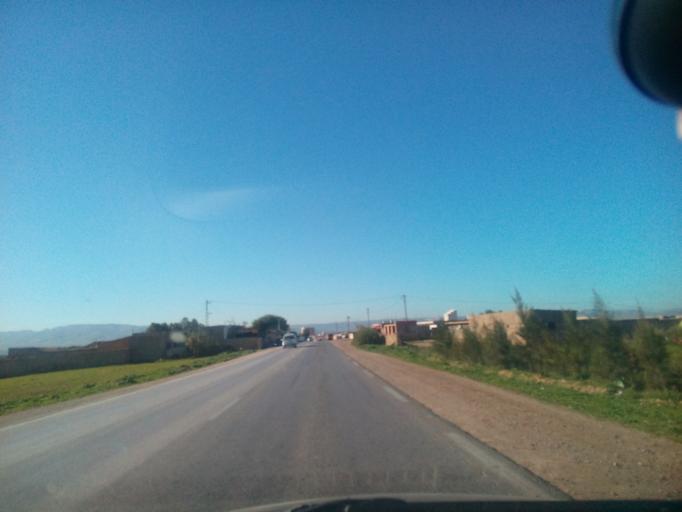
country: DZ
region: Relizane
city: Relizane
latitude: 35.8972
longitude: 0.5926
